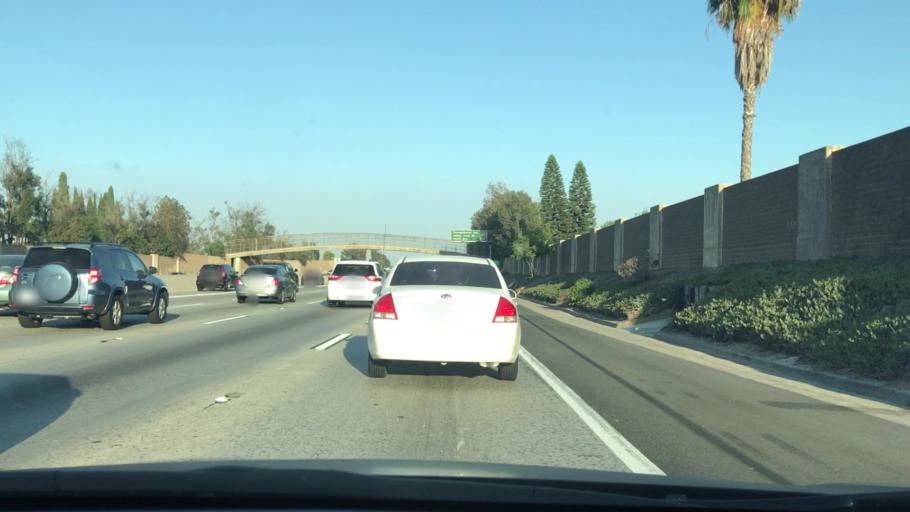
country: US
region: California
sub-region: Orange County
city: La Palma
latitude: 33.8625
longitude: -118.0434
